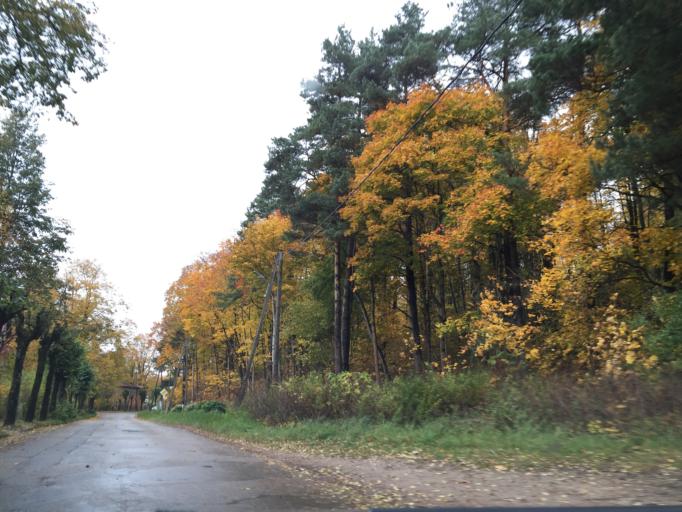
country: LV
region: Ogre
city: Ogre
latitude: 56.8119
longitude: 24.6156
